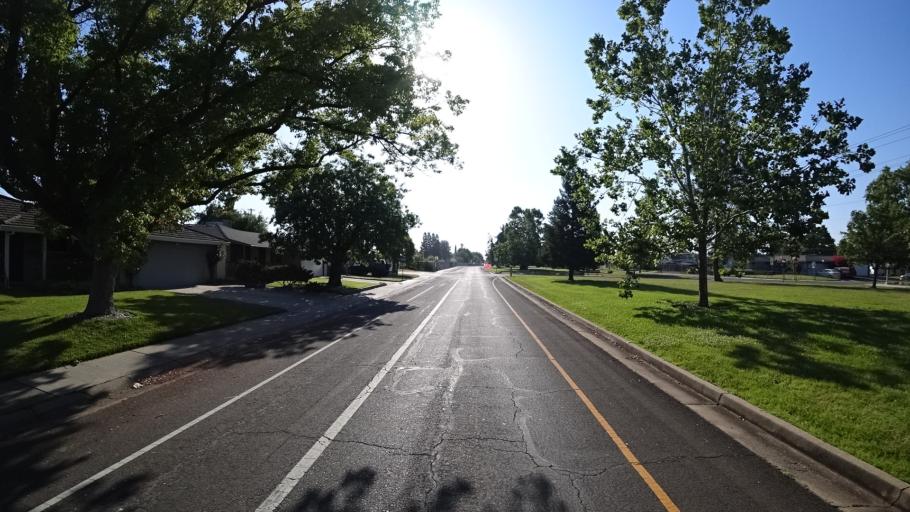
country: US
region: California
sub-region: Sacramento County
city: Florin
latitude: 38.5324
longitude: -121.4197
